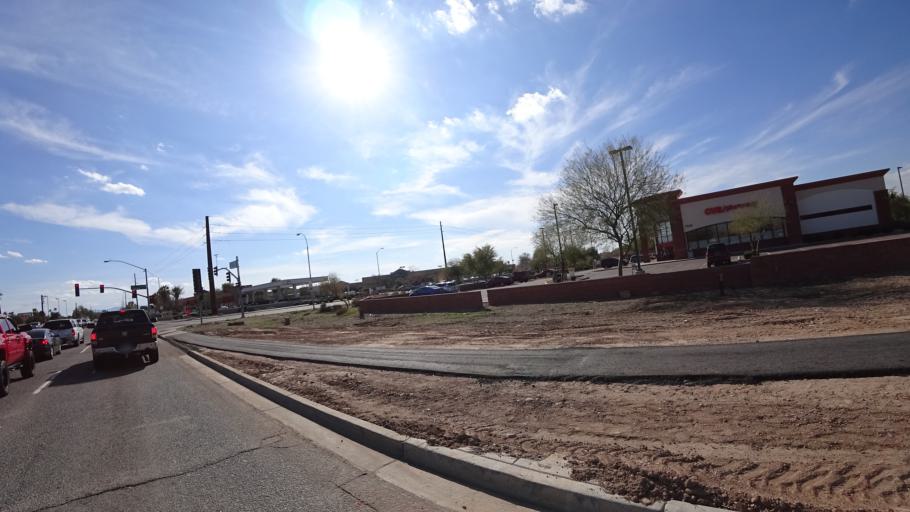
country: US
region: Arizona
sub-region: Maricopa County
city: Peoria
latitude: 33.5964
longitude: -112.2203
